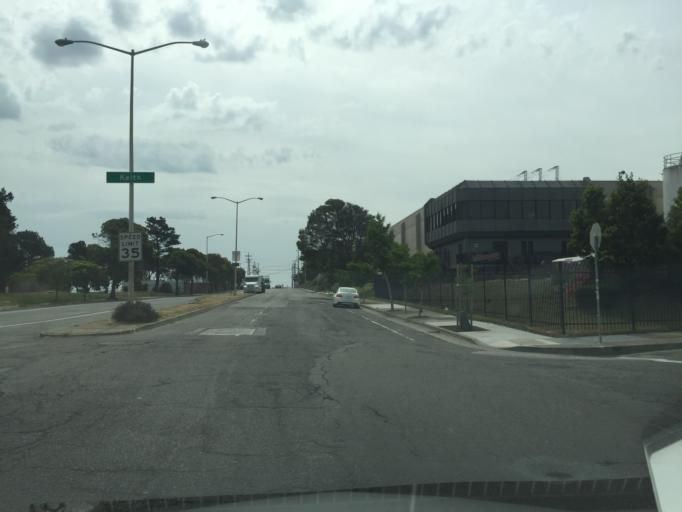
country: US
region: California
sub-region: San Francisco County
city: San Francisco
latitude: 37.7388
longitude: -122.3812
